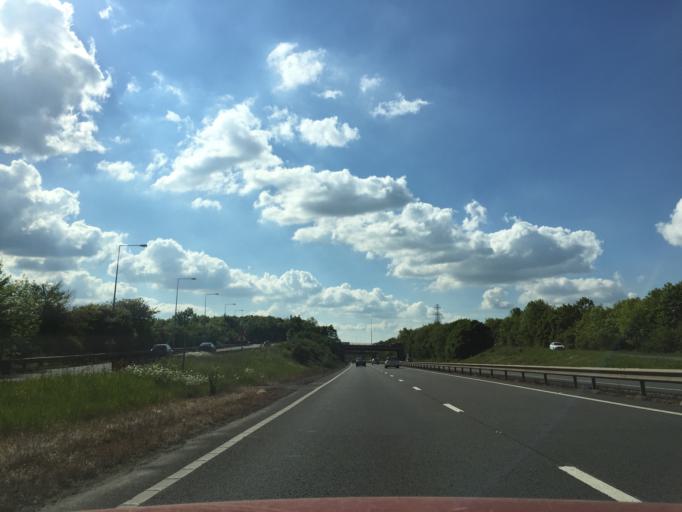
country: GB
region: England
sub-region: Milton Keynes
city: Bradwell
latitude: 52.0460
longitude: -0.7996
